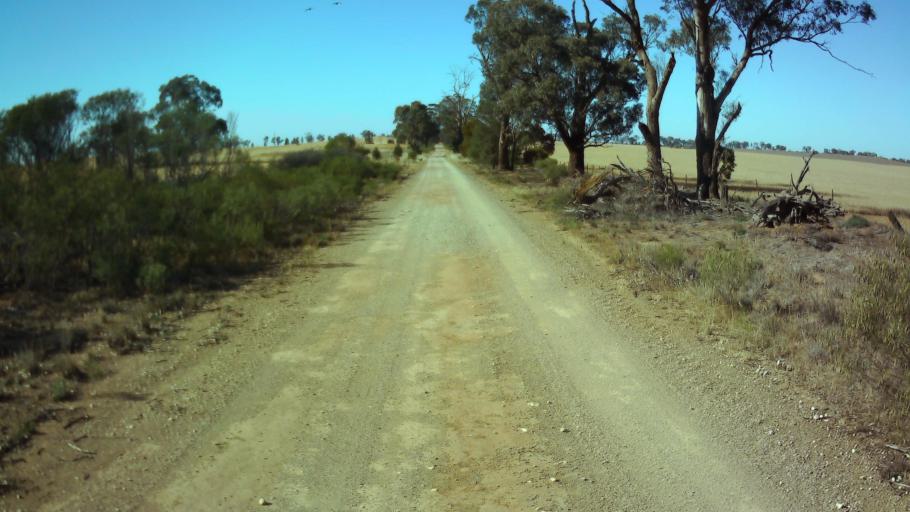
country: AU
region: New South Wales
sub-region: Weddin
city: Grenfell
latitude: -33.8852
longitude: 147.8815
